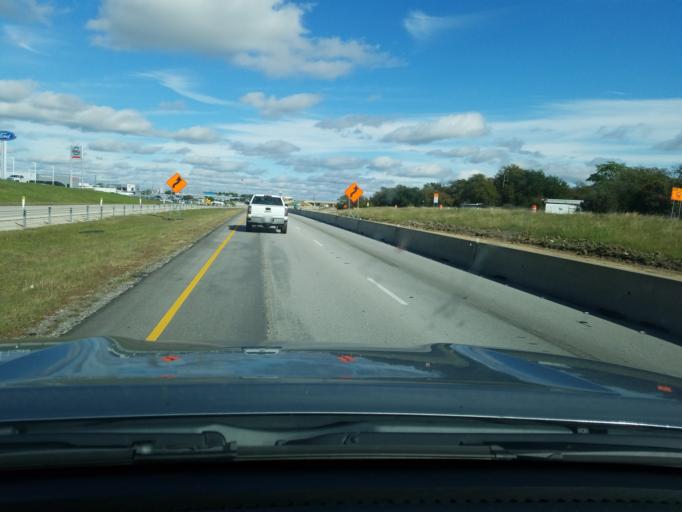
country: US
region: Texas
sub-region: Parker County
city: Hudson Oaks
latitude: 32.7539
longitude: -97.7077
